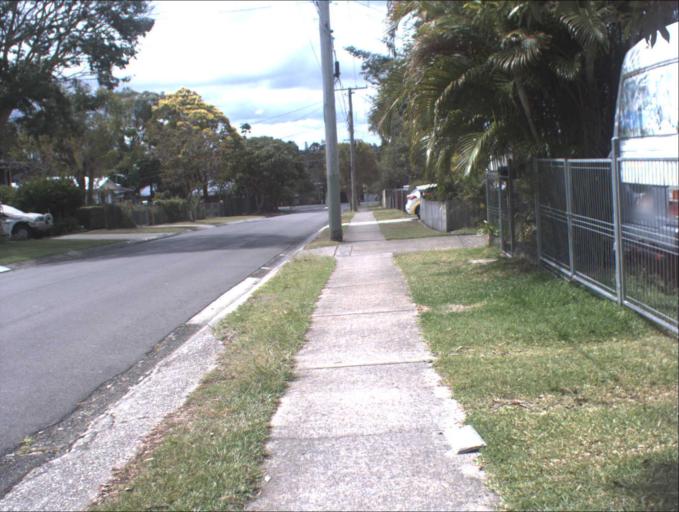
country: AU
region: Queensland
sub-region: Logan
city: Logan City
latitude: -27.6471
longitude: 153.1150
